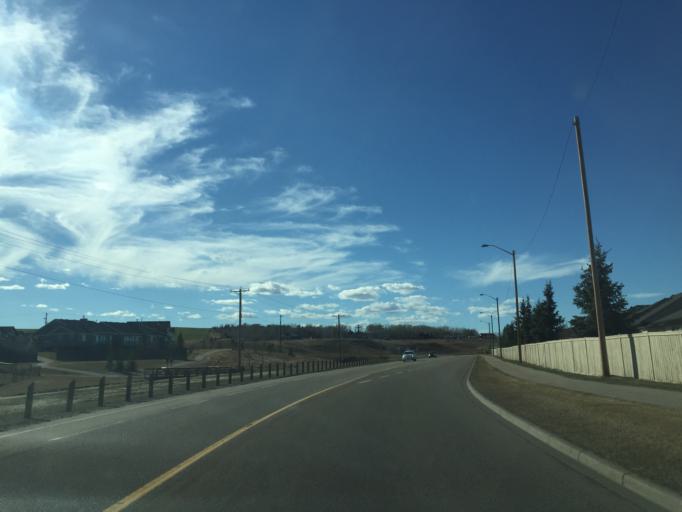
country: CA
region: Alberta
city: Airdrie
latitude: 51.2928
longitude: -114.0453
